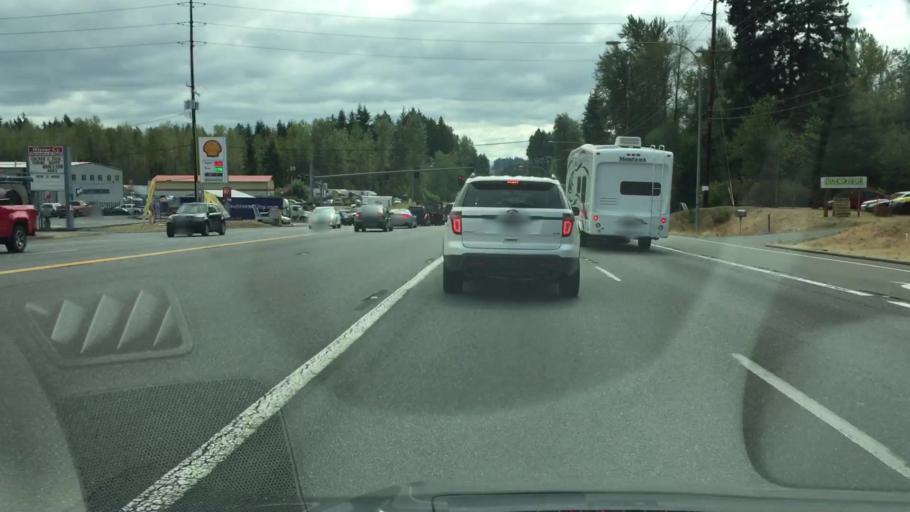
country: US
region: Washington
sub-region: Pierce County
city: Graham
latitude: 47.0759
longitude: -122.2943
